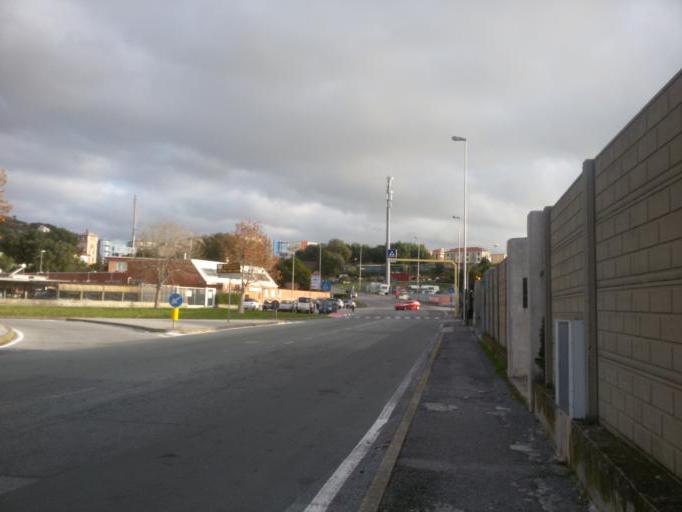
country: IT
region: Liguria
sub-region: Provincia di Savona
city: Savona
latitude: 44.2991
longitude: 8.4557
